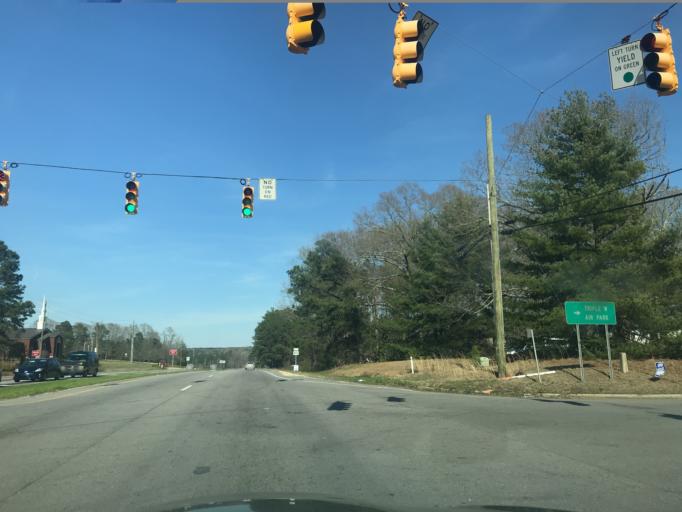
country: US
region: North Carolina
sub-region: Wake County
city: Fuquay-Varina
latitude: 35.6247
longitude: -78.7234
